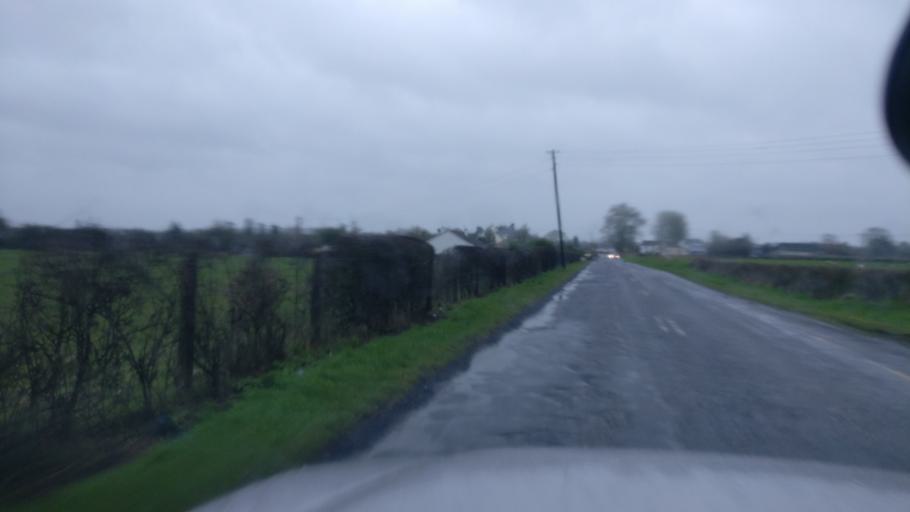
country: IE
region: Connaught
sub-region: County Galway
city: Ballinasloe
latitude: 53.2490
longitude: -8.1763
